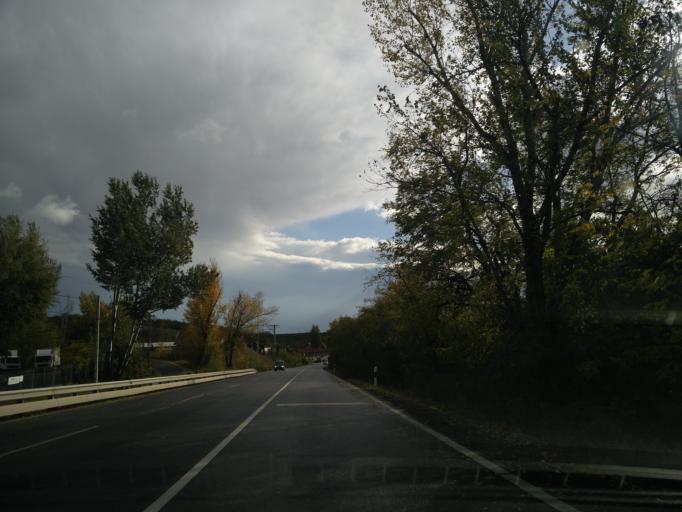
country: HU
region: Pest
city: Kerepes
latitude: 47.5712
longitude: 19.2927
